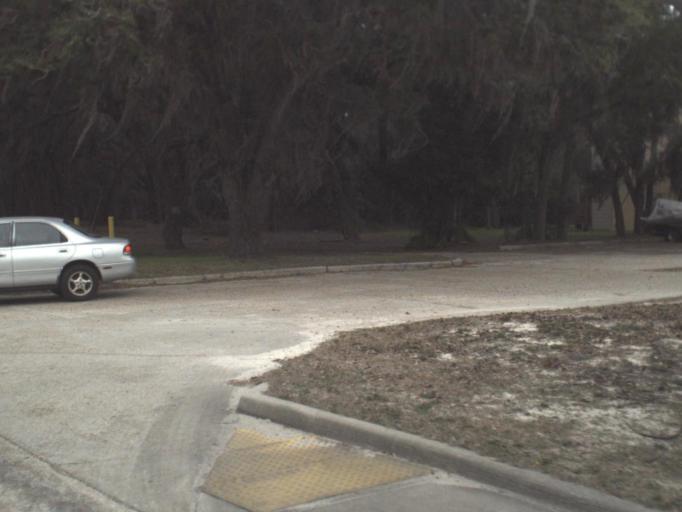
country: US
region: Florida
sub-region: Bay County
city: Parker
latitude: 30.1171
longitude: -85.5968
